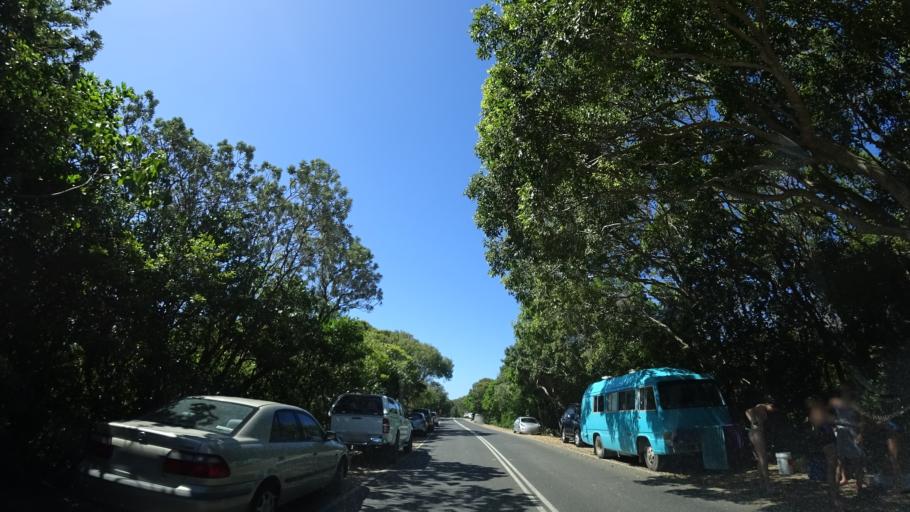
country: AU
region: Queensland
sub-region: Sunshine Coast
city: Mooloolaba
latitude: -26.6383
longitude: 153.1010
